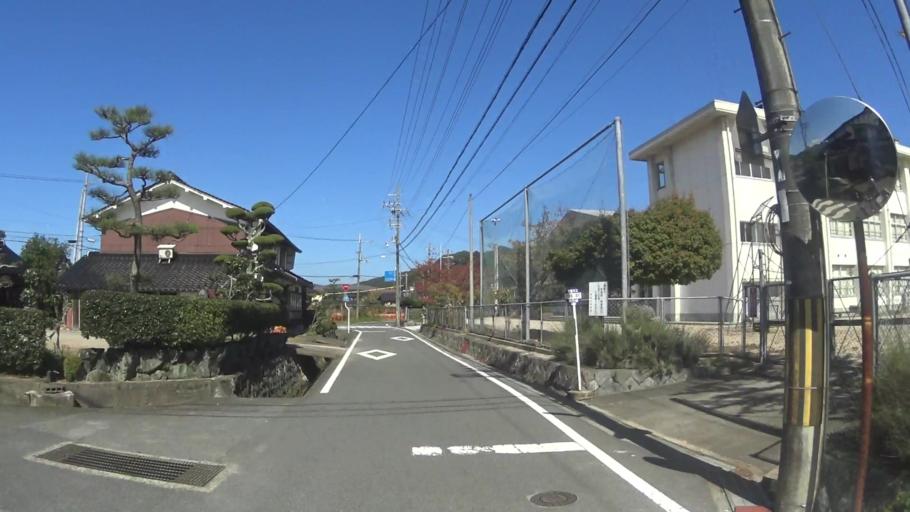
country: JP
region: Hyogo
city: Toyooka
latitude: 35.5892
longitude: 134.9314
